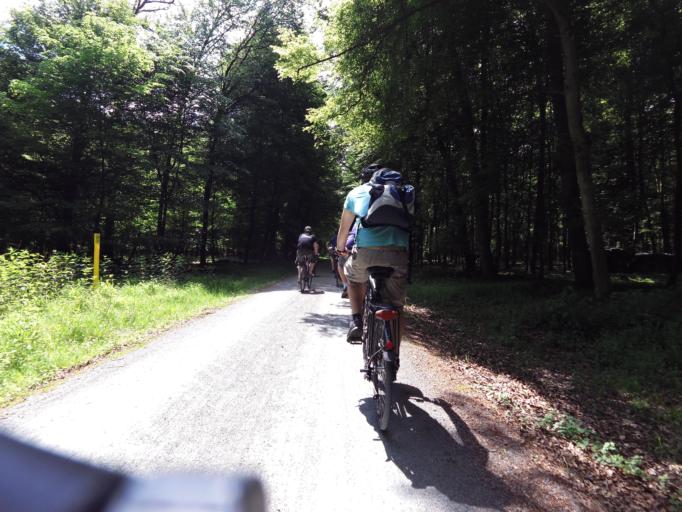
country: DE
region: Hesse
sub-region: Regierungsbezirk Darmstadt
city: Nauheim
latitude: 49.9684
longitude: 8.5058
